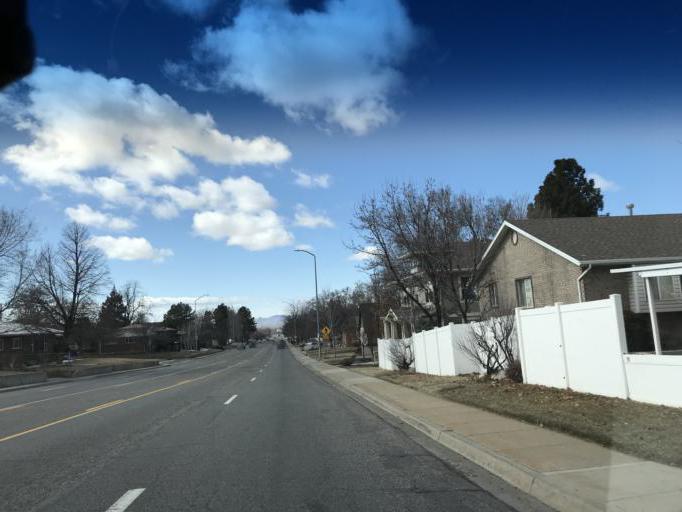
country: US
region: Utah
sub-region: Davis County
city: Bountiful
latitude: 40.8843
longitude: -111.8739
